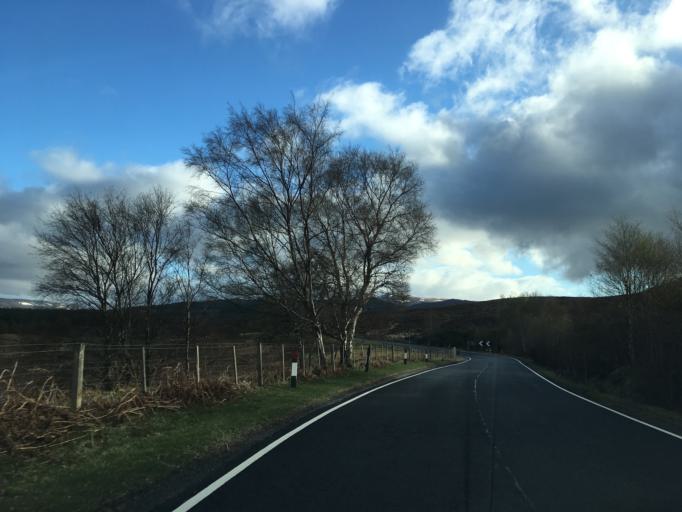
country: GB
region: Scotland
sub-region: Highland
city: Kingussie
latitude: 56.9937
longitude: -4.2485
